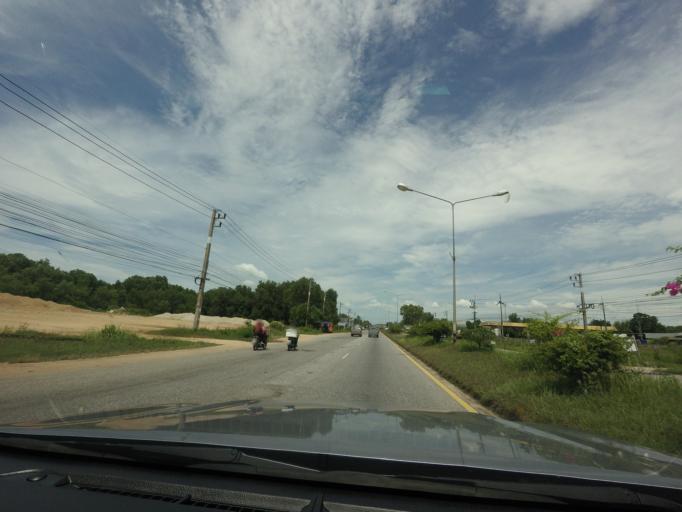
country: TH
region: Songkhla
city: Singhanakhon
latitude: 7.2447
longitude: 100.5419
